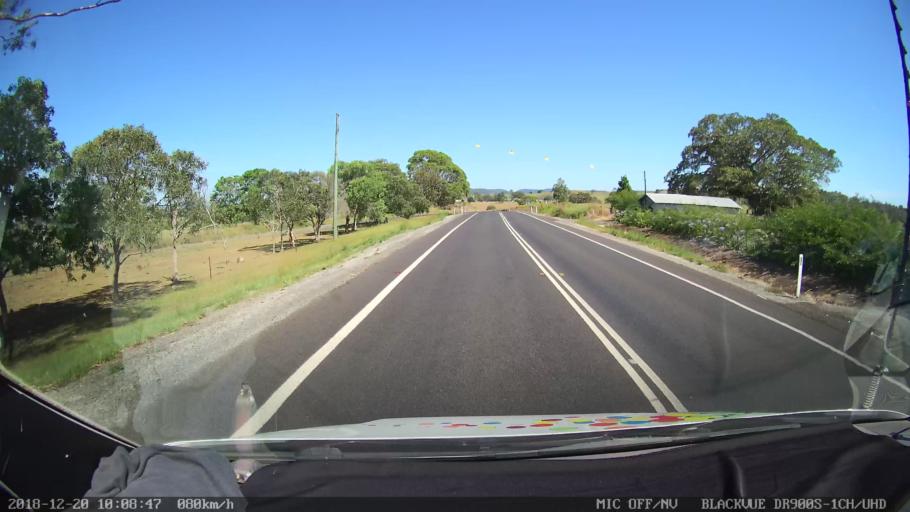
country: AU
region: New South Wales
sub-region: Lismore Municipality
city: Lismore
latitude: -28.8805
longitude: 153.1959
